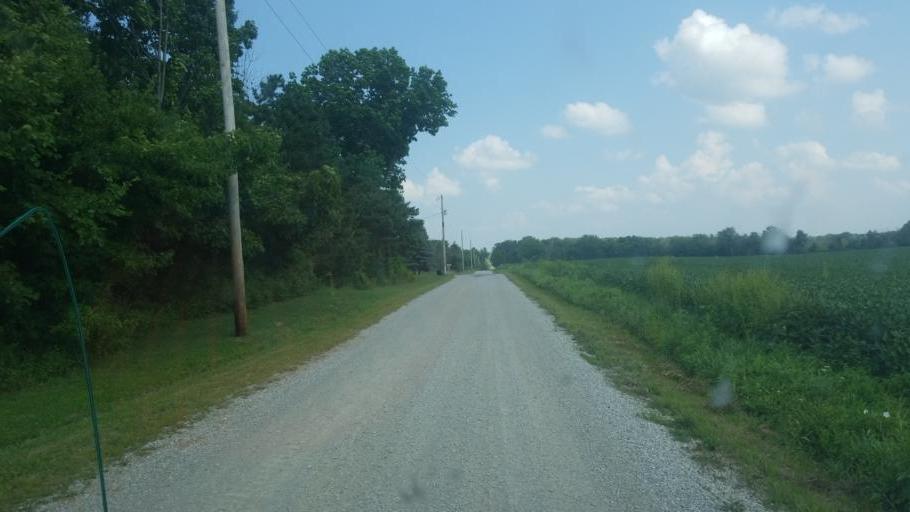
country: US
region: Ohio
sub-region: Huron County
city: New London
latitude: 41.0495
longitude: -82.3735
